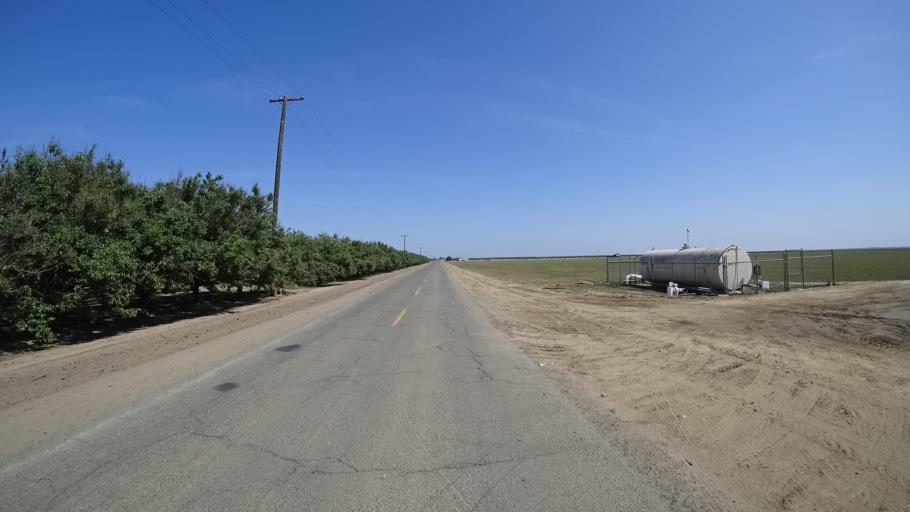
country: US
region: California
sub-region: Kings County
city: Kettleman City
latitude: 36.0684
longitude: -120.0037
